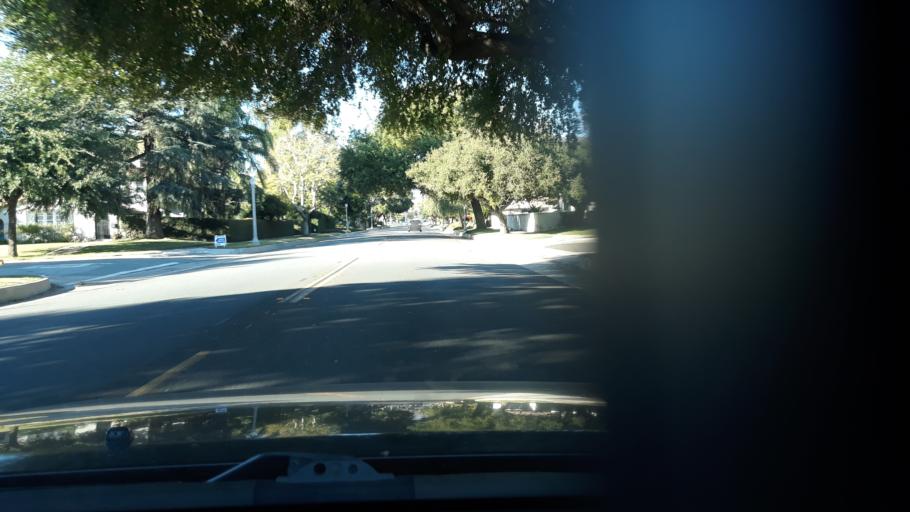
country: US
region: California
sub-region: Los Angeles County
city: San Marino
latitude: 34.1178
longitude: -118.1053
